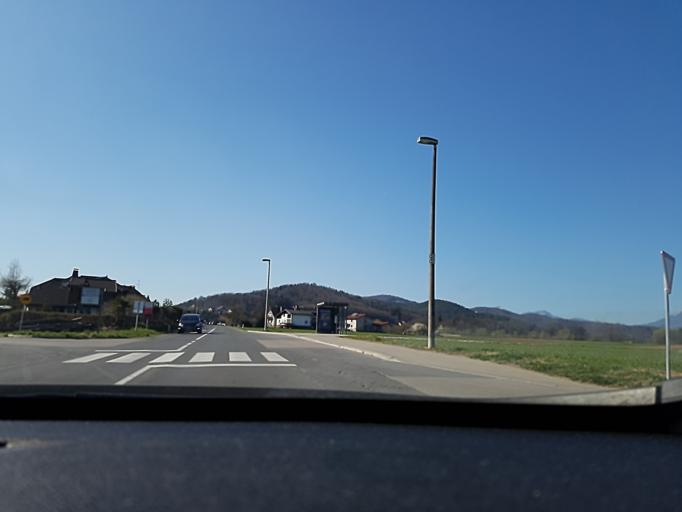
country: SI
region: Trzin
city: Trzin
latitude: 46.1003
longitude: 14.5538
